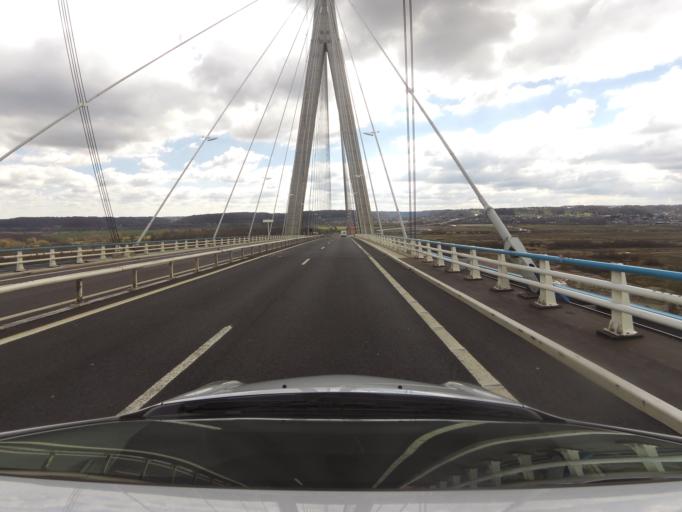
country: FR
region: Lower Normandy
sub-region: Departement du Calvados
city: La Riviere-Saint-Sauveur
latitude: 49.4297
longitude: 0.2743
